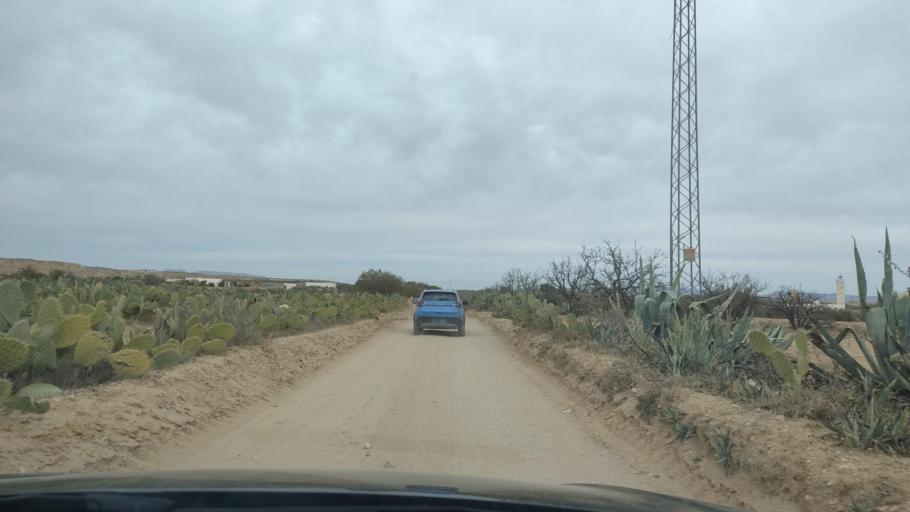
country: TN
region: Al Qasrayn
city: Kasserine
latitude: 35.2637
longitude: 8.9314
